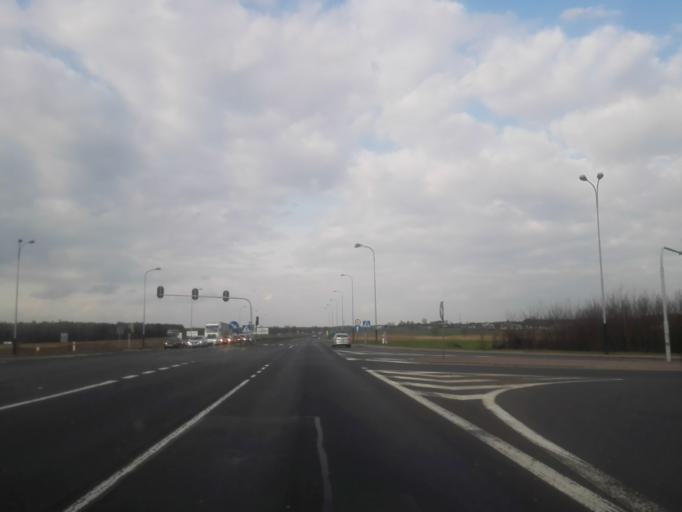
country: PL
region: Lodz Voivodeship
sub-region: Powiat radomszczanski
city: Kamiensk
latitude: 51.2114
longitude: 19.4865
